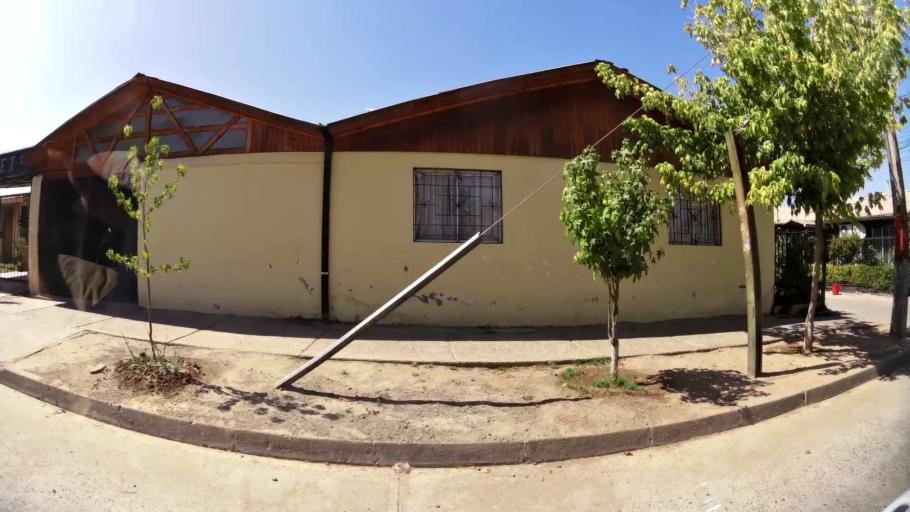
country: CL
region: Maule
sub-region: Provincia de Talca
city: Talca
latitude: -35.4167
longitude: -71.6383
